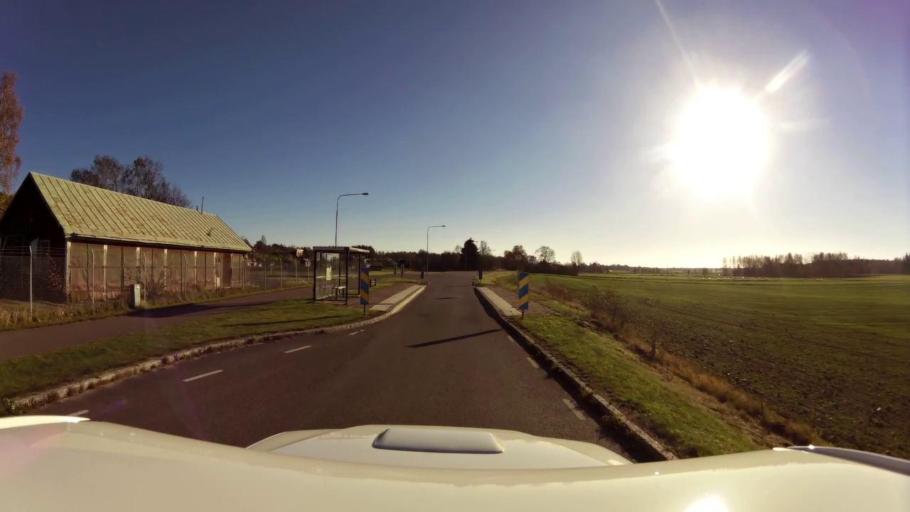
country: SE
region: OEstergoetland
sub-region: Linkopings Kommun
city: Malmslatt
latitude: 58.3651
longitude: 15.5599
